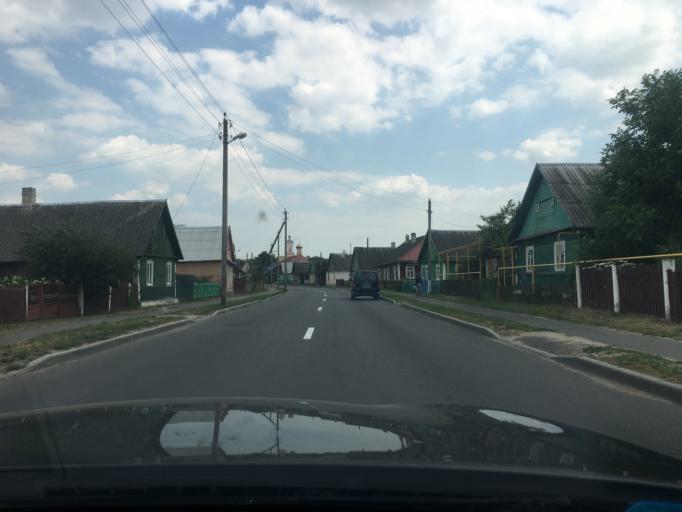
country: BY
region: Brest
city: Ruzhany
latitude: 52.8670
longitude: 24.8827
